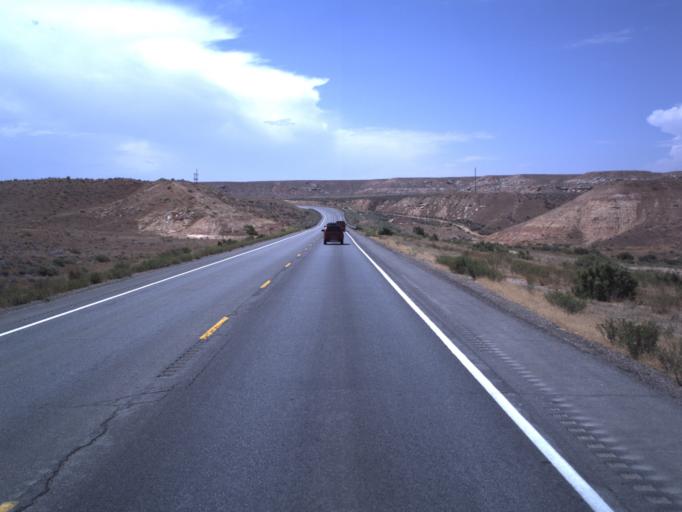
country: US
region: Utah
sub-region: Uintah County
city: Maeser
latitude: 40.3250
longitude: -109.6813
